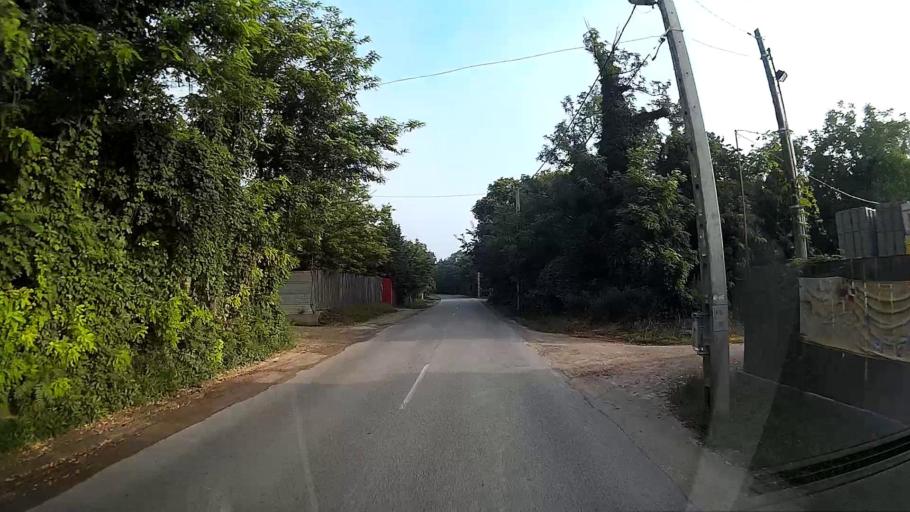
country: HU
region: Pest
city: Tahitotfalu
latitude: 47.7441
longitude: 19.0985
